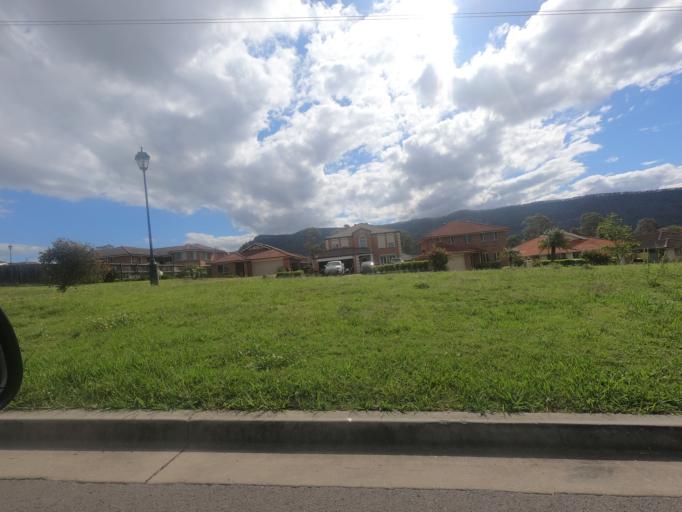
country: AU
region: New South Wales
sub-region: Wollongong
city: Dapto
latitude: -34.4892
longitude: 150.7685
